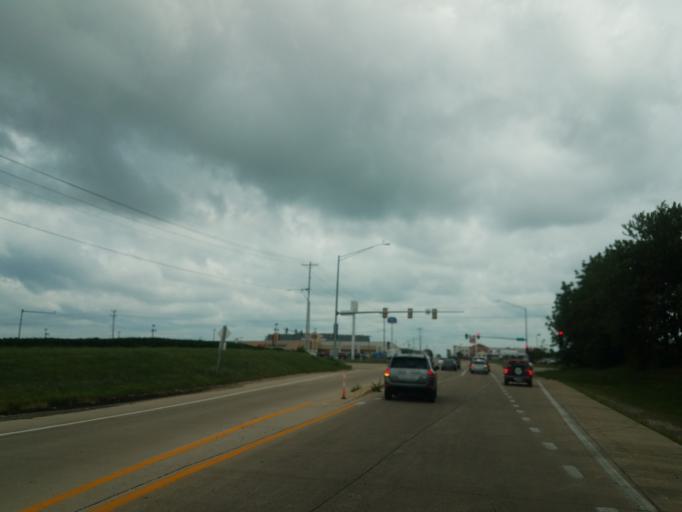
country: US
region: Illinois
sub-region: McLean County
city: Bloomington
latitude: 40.4853
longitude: -89.0371
